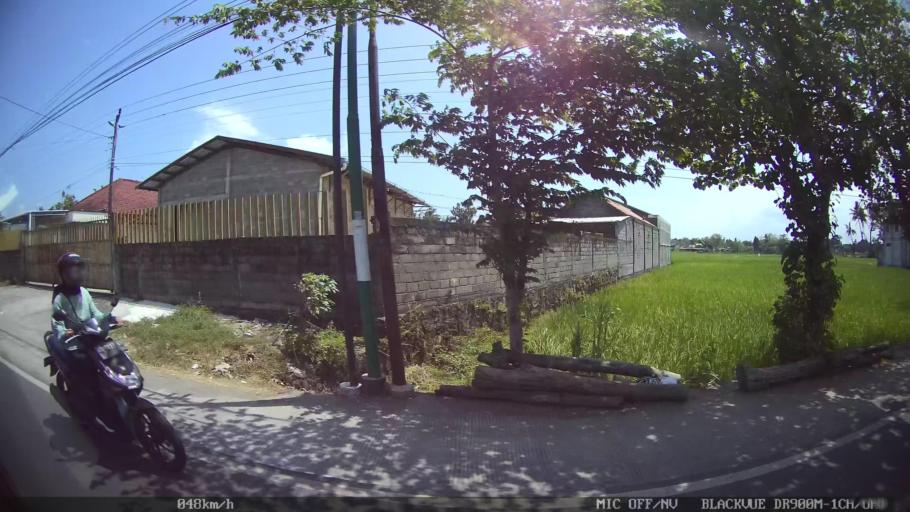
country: ID
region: Daerah Istimewa Yogyakarta
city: Pundong
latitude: -7.9347
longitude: 110.3738
